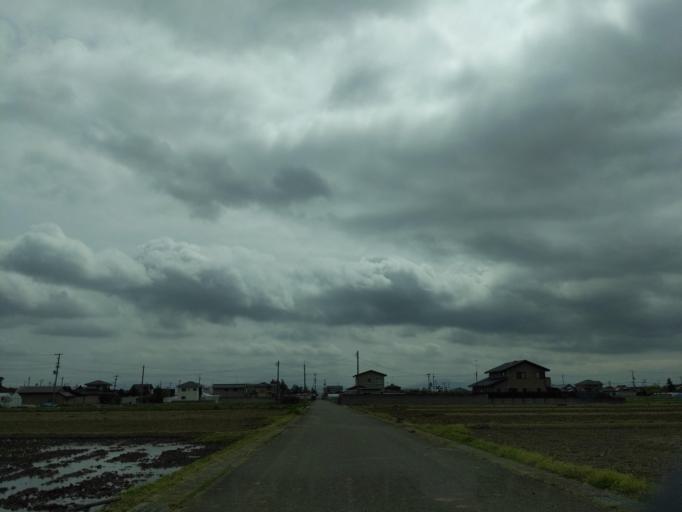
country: JP
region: Fukushima
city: Koriyama
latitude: 37.3742
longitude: 140.3229
